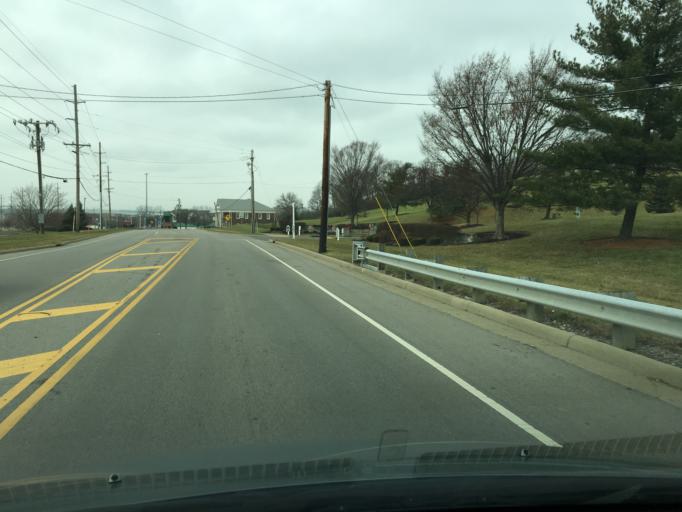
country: US
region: Ohio
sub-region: Butler County
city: Beckett Ridge
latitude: 39.3273
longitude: -84.4198
